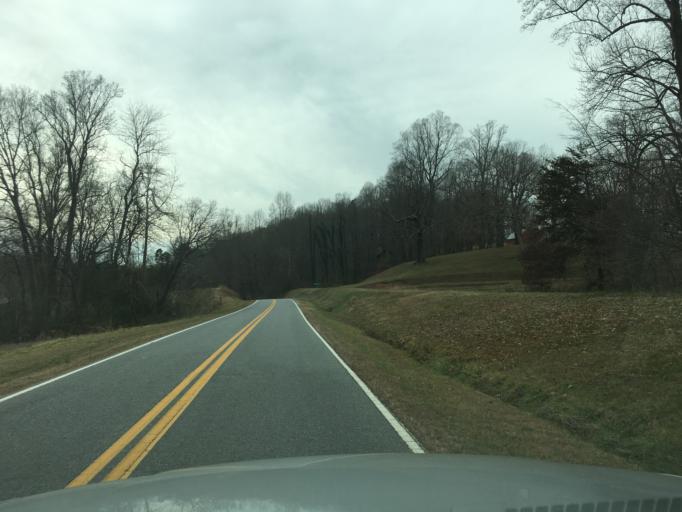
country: US
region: North Carolina
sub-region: McDowell County
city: West Marion
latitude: 35.6236
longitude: -81.9668
